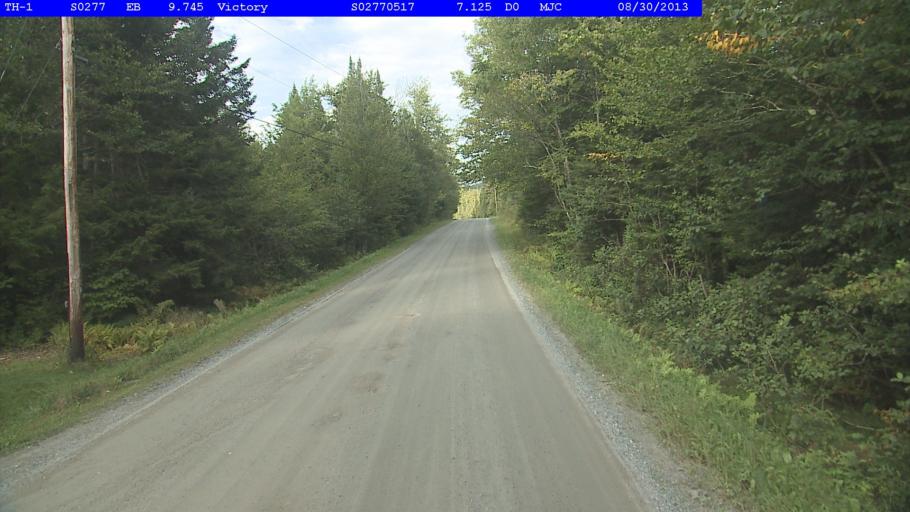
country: US
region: Vermont
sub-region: Caledonia County
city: Lyndonville
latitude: 44.5704
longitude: -71.7883
